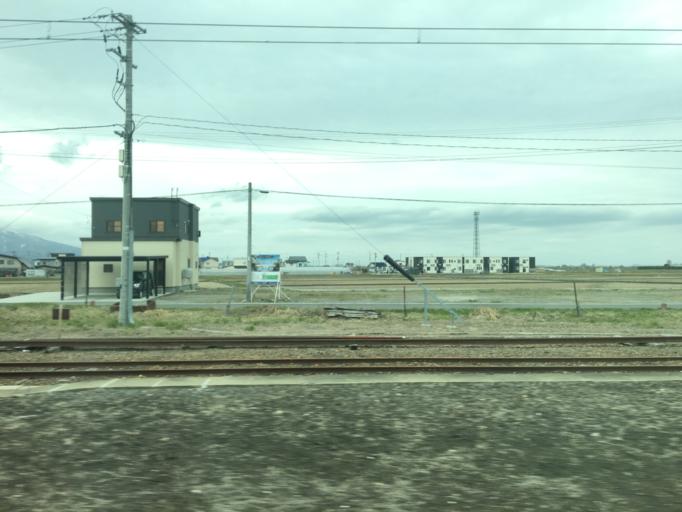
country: JP
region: Aomori
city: Kuroishi
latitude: 40.6481
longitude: 140.5225
